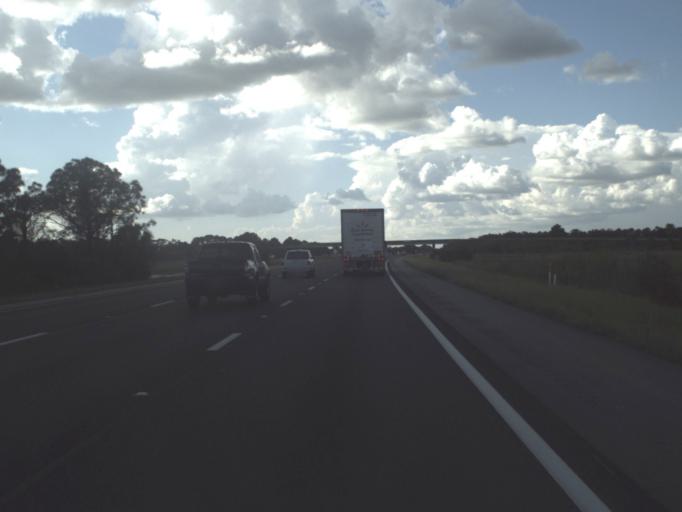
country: US
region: Florida
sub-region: Lee County
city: Suncoast Estates
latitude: 26.8074
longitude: -81.9274
